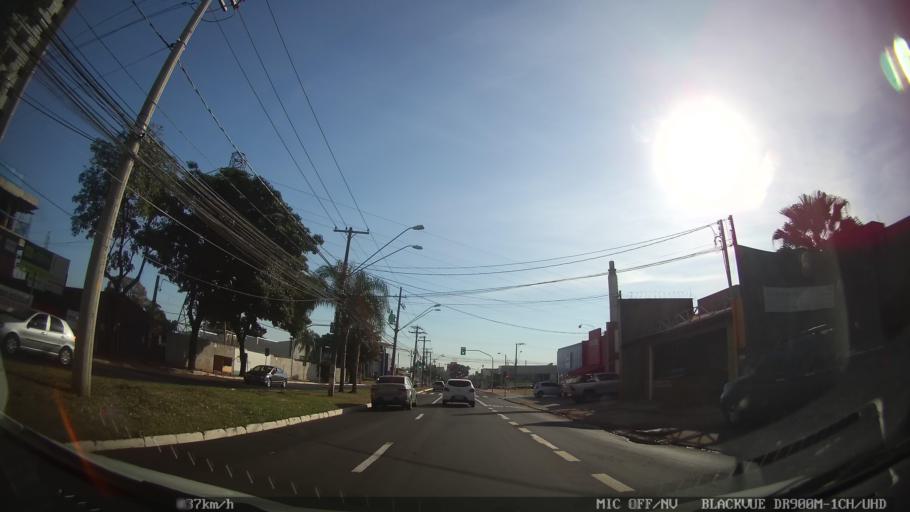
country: BR
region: Sao Paulo
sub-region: Ribeirao Preto
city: Ribeirao Preto
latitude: -21.1969
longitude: -47.8077
